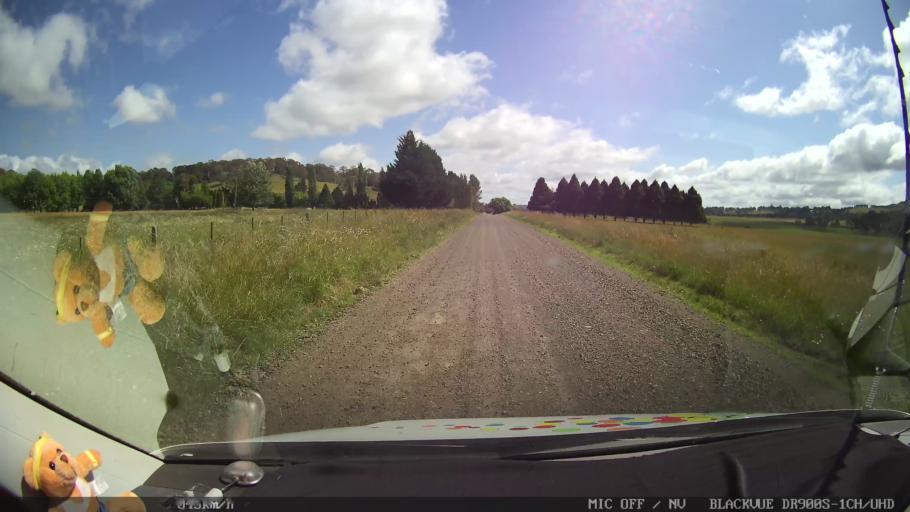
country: AU
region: New South Wales
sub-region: Glen Innes Severn
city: Glen Innes
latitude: -29.9614
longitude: 151.7004
